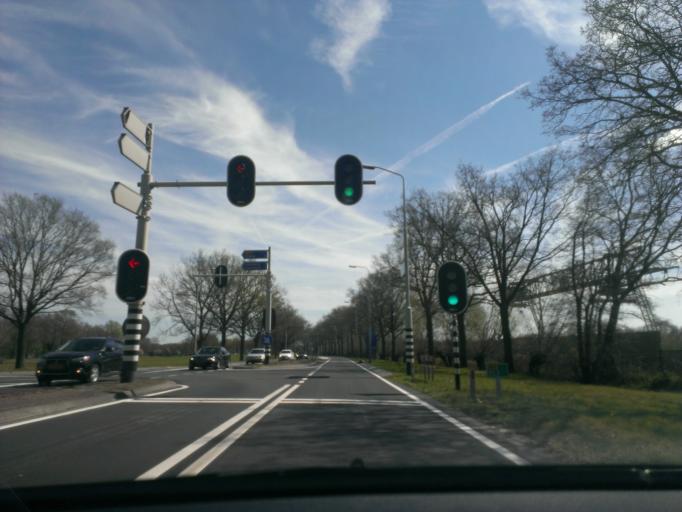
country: NL
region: Overijssel
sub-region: Gemeente Raalte
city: Raalte
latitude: 52.3873
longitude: 6.2888
